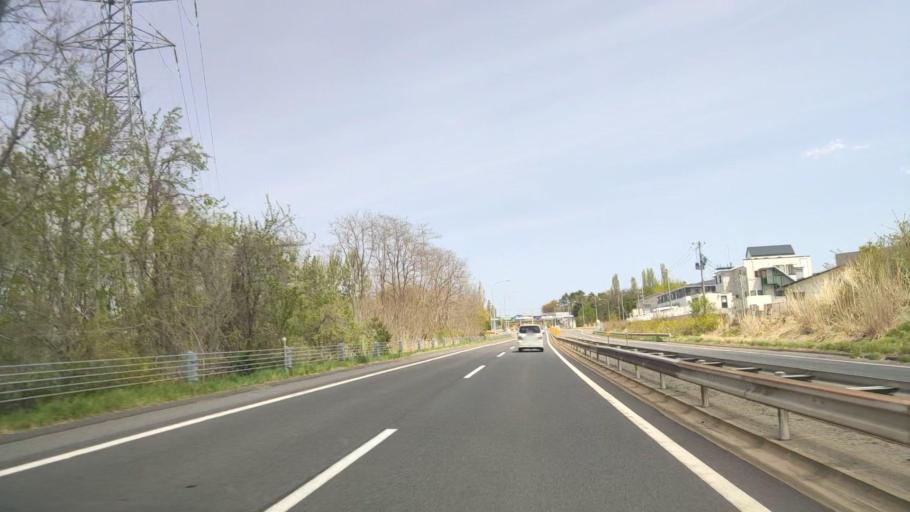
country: JP
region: Aomori
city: Hachinohe
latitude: 40.4837
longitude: 141.4609
